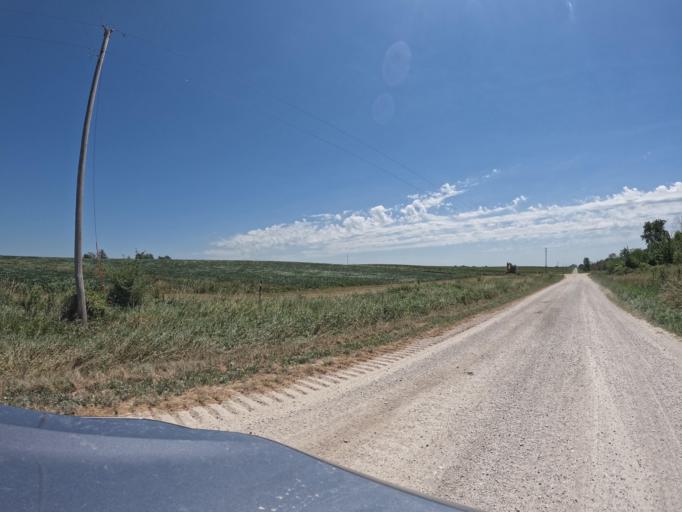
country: US
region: Iowa
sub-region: Keokuk County
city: Sigourney
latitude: 41.4099
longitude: -92.3163
